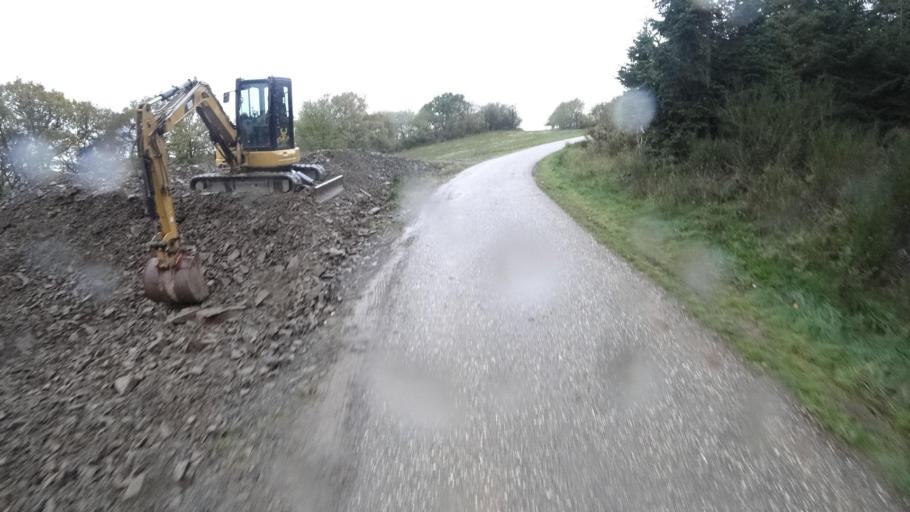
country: DE
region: Rheinland-Pfalz
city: Kirchsahr
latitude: 50.5235
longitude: 6.8955
